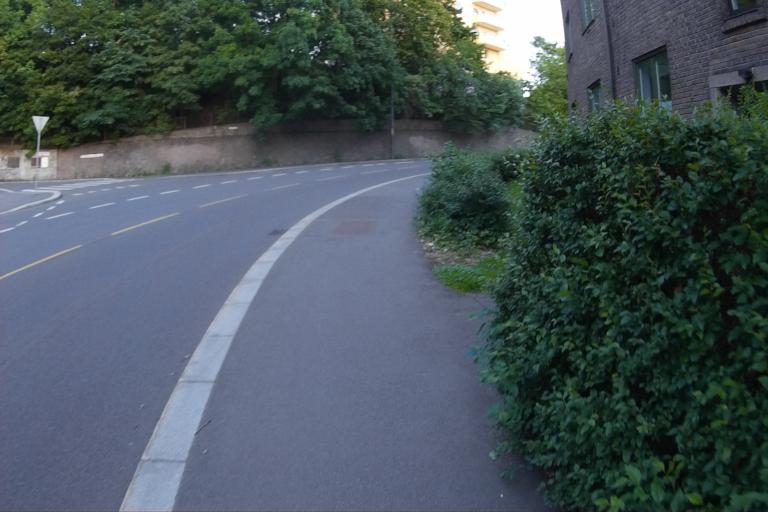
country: NO
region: Oslo
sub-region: Oslo
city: Oslo
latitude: 59.9255
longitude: 10.7781
